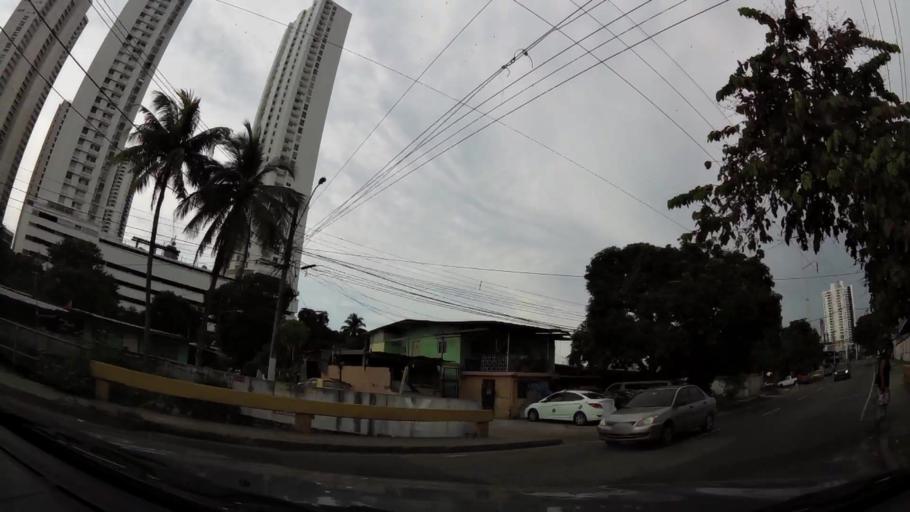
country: PA
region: Panama
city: Panama
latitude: 9.0049
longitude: -79.4955
